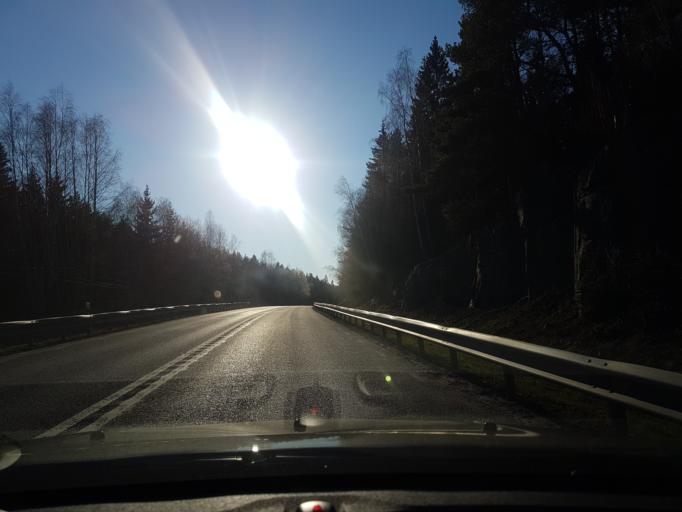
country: SE
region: Uppsala
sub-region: Enkopings Kommun
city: Orsundsbro
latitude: 59.8806
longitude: 17.2435
